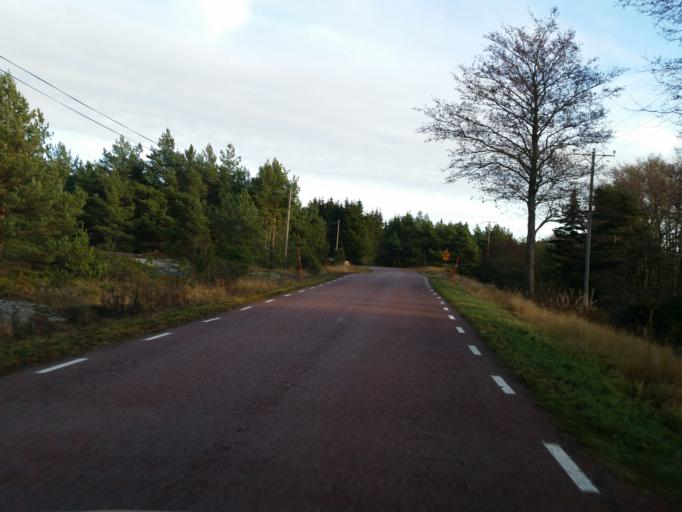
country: AX
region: Alands skaergard
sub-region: Kumlinge
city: Kumlinge
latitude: 60.2553
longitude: 20.7530
